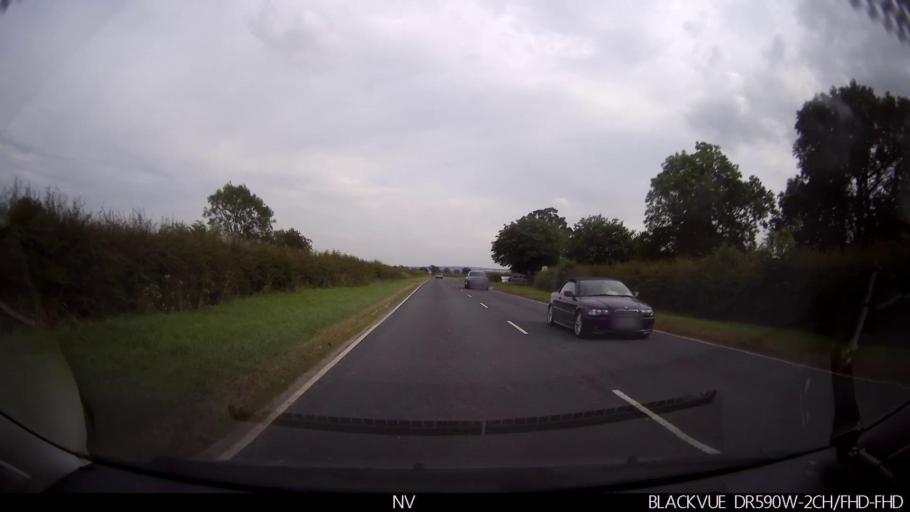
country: GB
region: England
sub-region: North Yorkshire
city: Marishes
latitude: 54.1980
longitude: -0.7675
